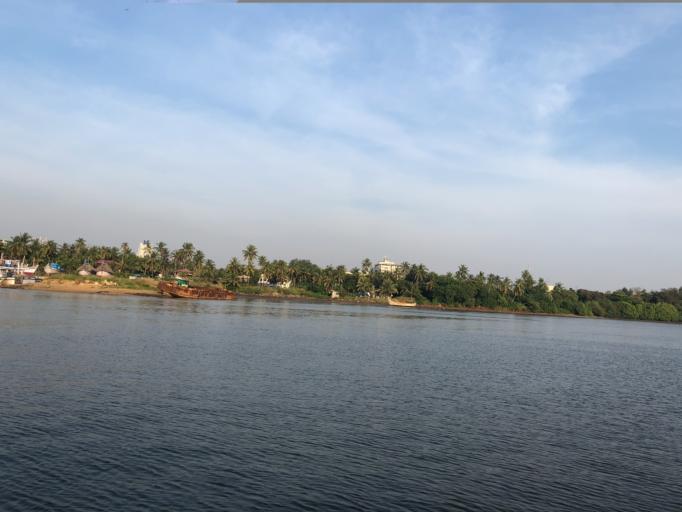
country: IN
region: Karnataka
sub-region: Dakshina Kannada
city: Mangalore
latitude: 12.8860
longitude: 74.8191
